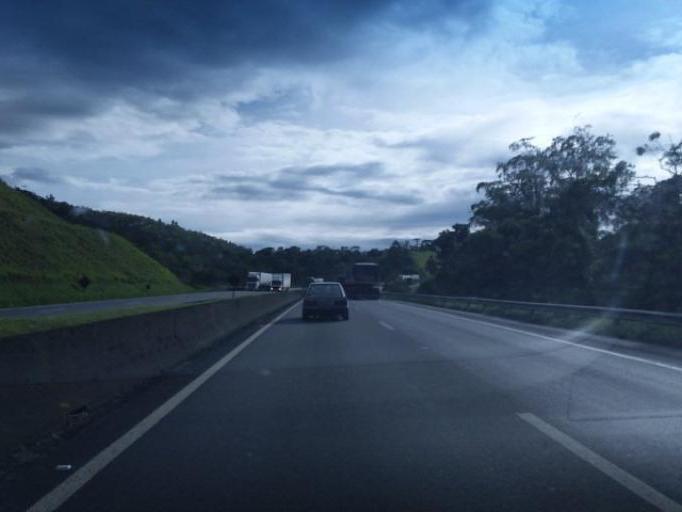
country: BR
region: Parana
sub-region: Antonina
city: Antonina
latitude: -25.1057
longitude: -48.7399
